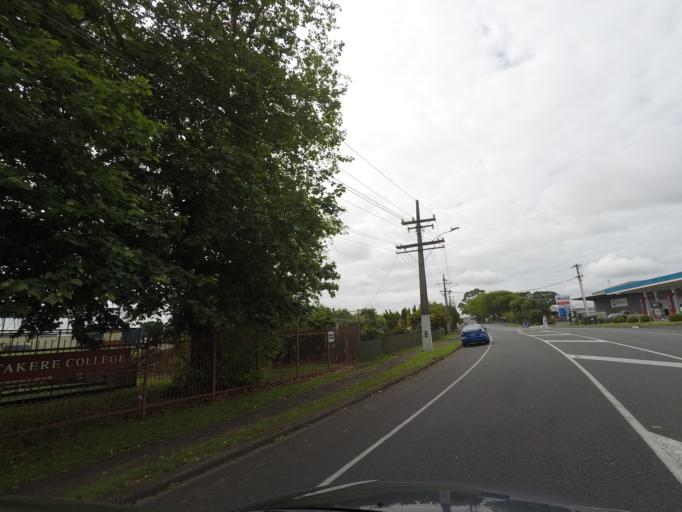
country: NZ
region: Auckland
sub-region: Auckland
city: Rosebank
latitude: -36.8678
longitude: 174.6166
